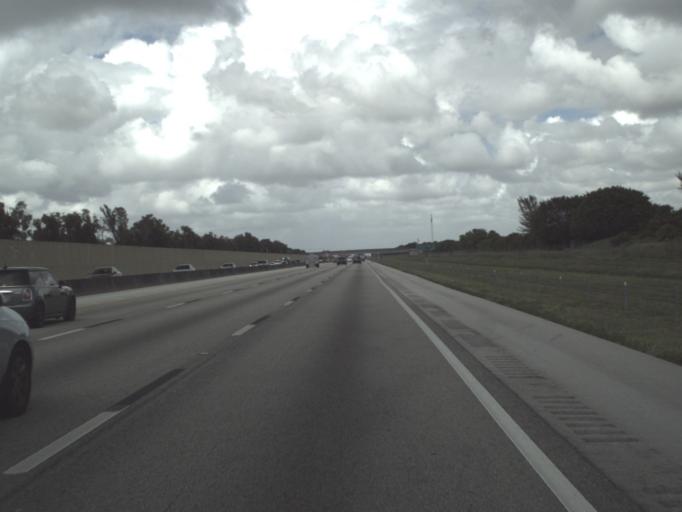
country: US
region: Florida
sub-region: Palm Beach County
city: Boca Del Mar
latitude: 26.3853
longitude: -80.1709
